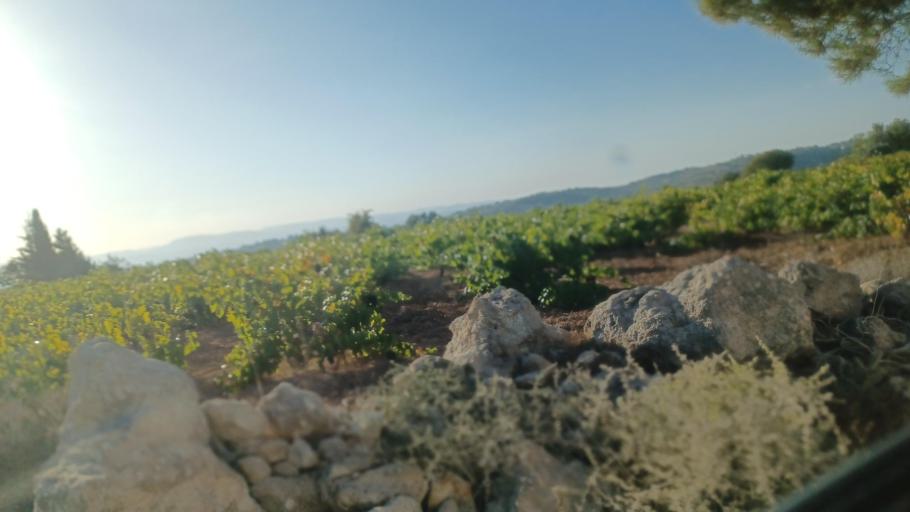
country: CY
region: Pafos
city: Mesogi
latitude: 34.8554
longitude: 32.4715
